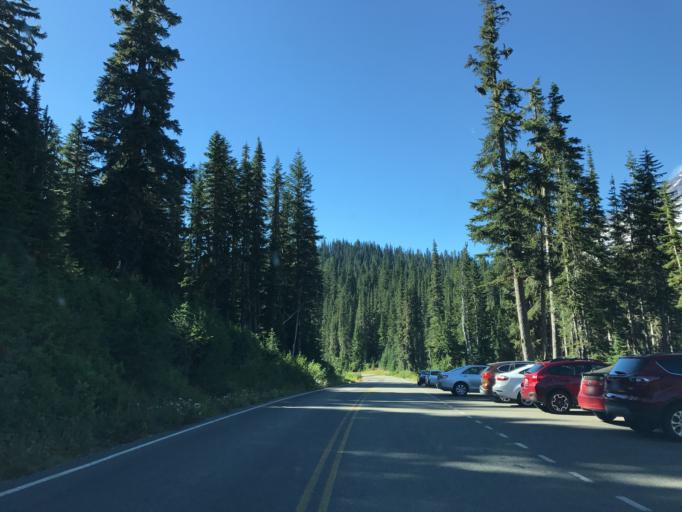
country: US
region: Washington
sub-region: Pierce County
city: Buckley
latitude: 46.7685
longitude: -121.7318
